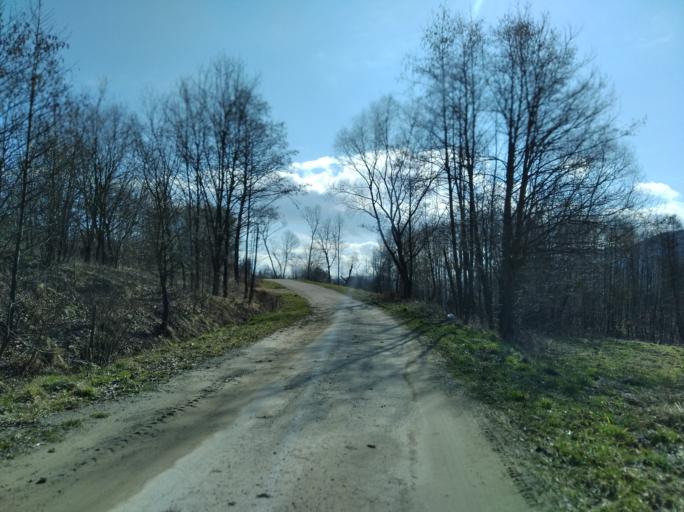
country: PL
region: Subcarpathian Voivodeship
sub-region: Powiat strzyzowski
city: Wysoka Strzyzowska
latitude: 49.8069
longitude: 21.7516
